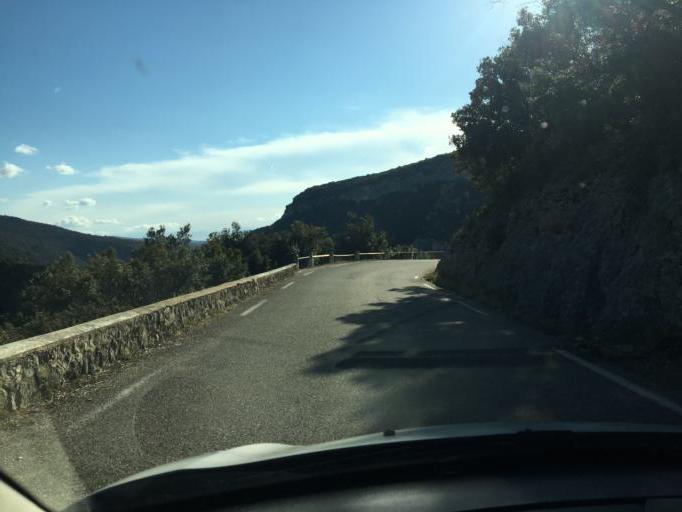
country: FR
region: Provence-Alpes-Cote d'Azur
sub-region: Departement du Vaucluse
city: Villes-sur-Auzon
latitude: 44.0665
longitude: 5.3093
